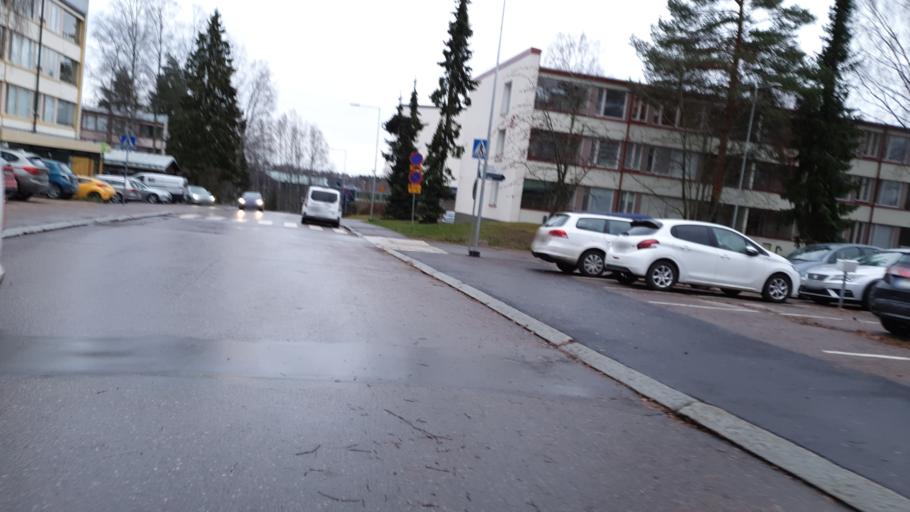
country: FI
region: Uusimaa
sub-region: Helsinki
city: Teekkarikylae
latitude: 60.2701
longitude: 24.8706
